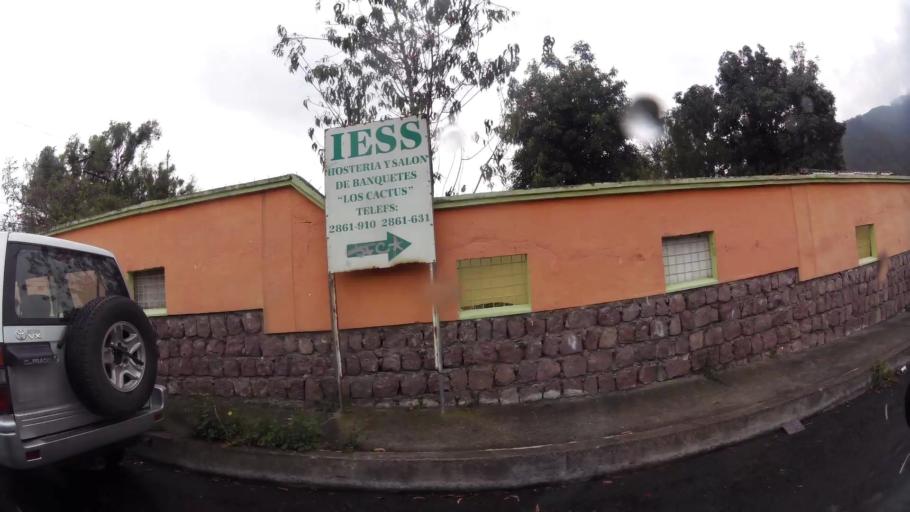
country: EC
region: Pichincha
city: Sangolqui
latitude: -0.2866
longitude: -78.4461
